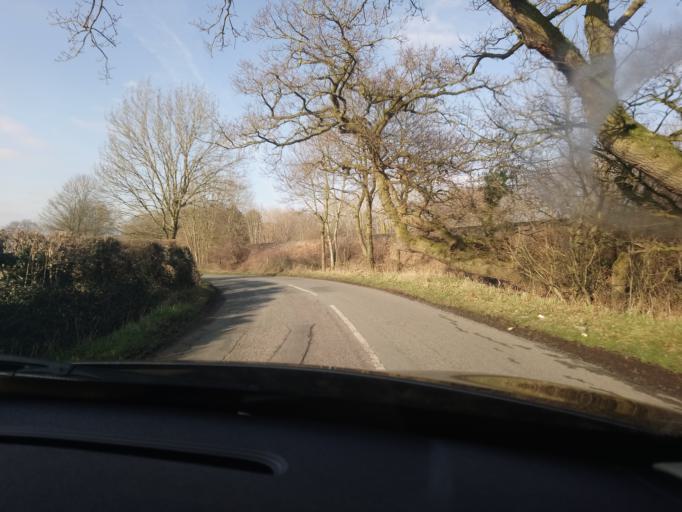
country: GB
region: England
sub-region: Shropshire
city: Bicton
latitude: 52.7598
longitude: -2.7774
